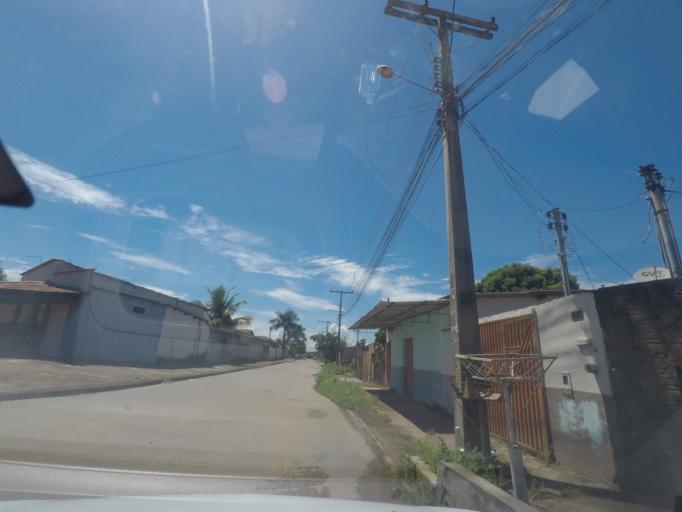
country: BR
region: Goias
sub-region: Aparecida De Goiania
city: Aparecida de Goiania
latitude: -16.7737
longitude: -49.3247
